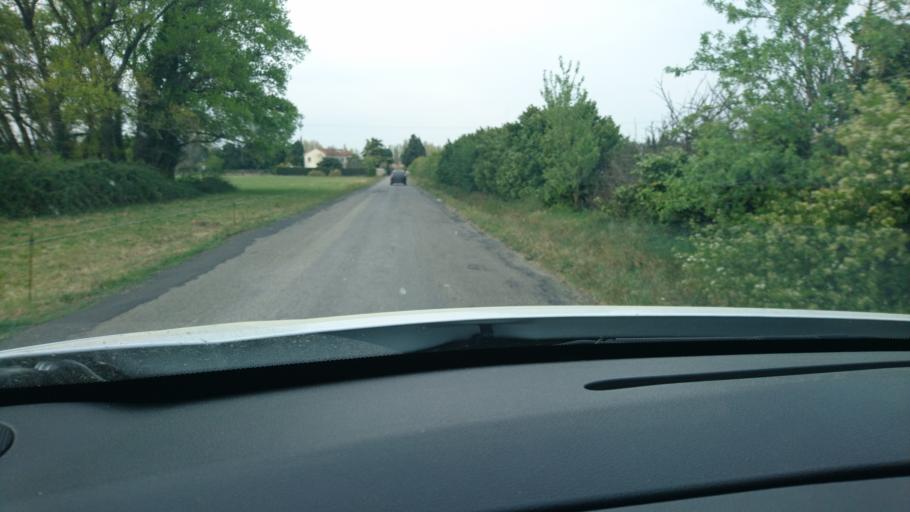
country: FR
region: Provence-Alpes-Cote d'Azur
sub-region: Departement du Vaucluse
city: Montfavet
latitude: 43.9497
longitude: 4.8816
